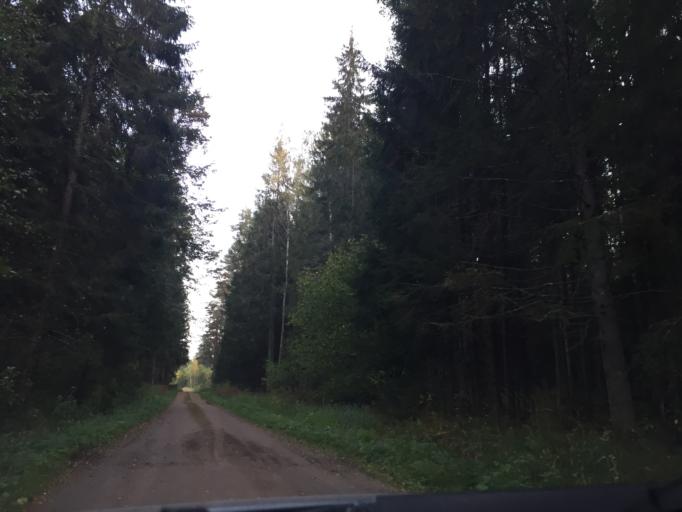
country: LV
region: Ikskile
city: Ikskile
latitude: 56.9298
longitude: 24.4912
